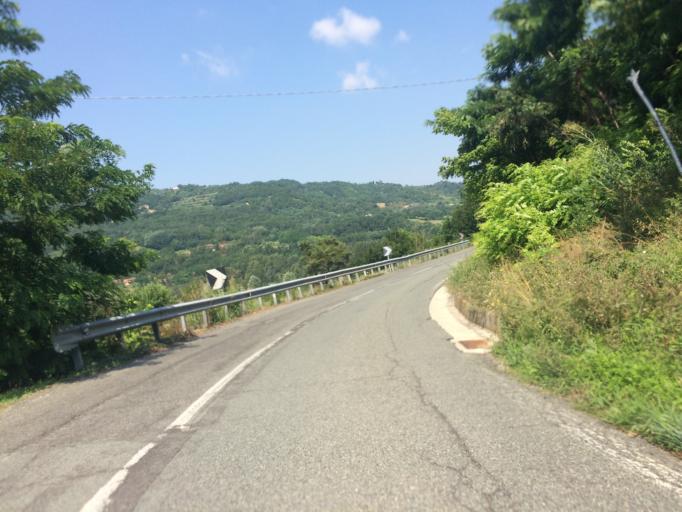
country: IT
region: Piedmont
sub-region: Provincia di Alessandria
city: Castelletto d'Erro
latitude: 44.6251
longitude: 8.4154
